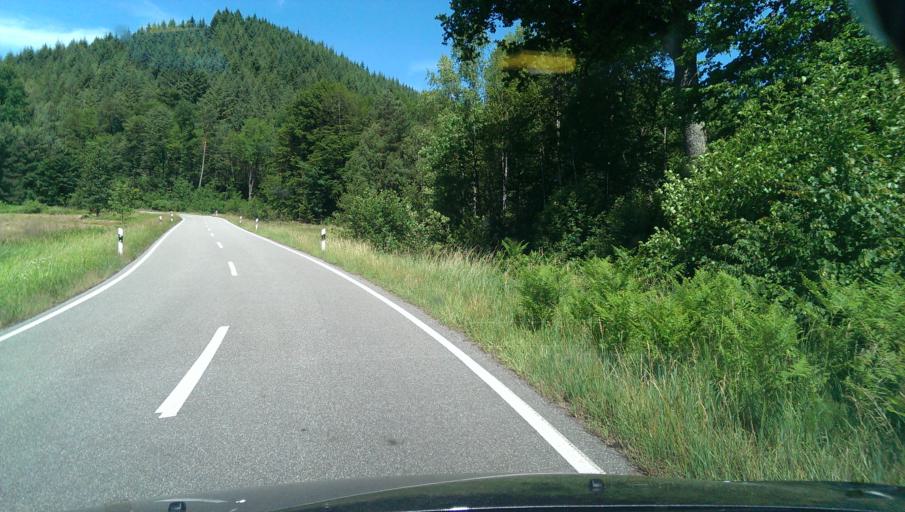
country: DE
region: Rheinland-Pfalz
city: Fischbach
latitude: 49.0830
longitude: 7.7357
